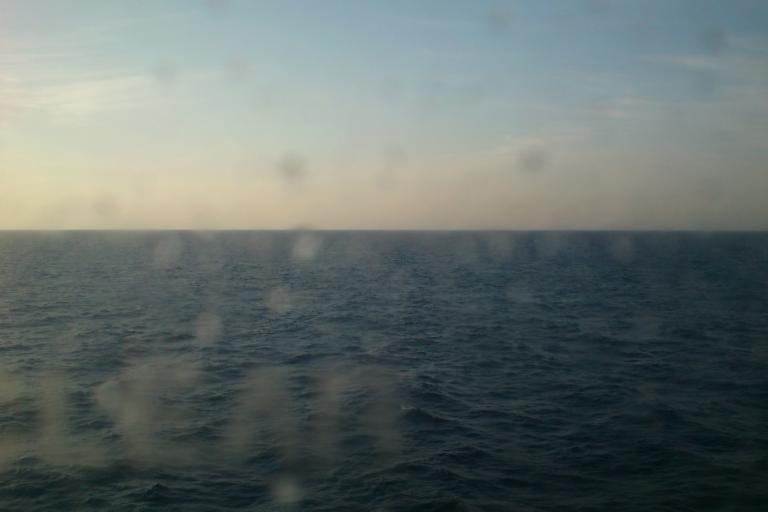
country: JP
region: Ishikawa
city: Nanao
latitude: 37.7092
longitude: 136.3824
